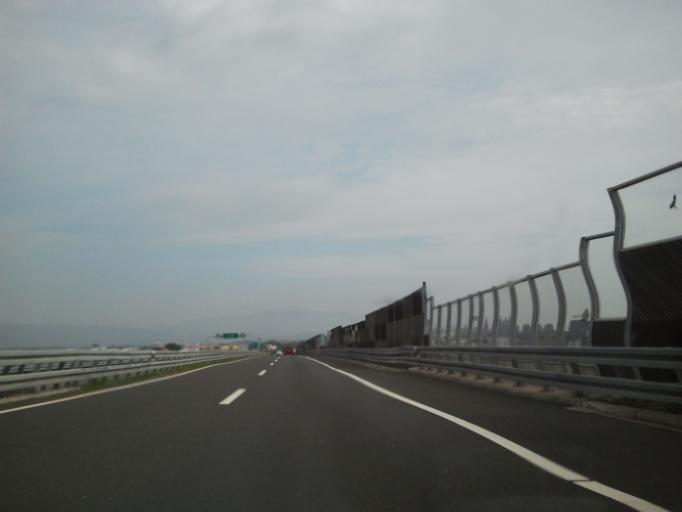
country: HR
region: Grad Zagreb
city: Brezovica
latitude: 45.7389
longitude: 15.8789
